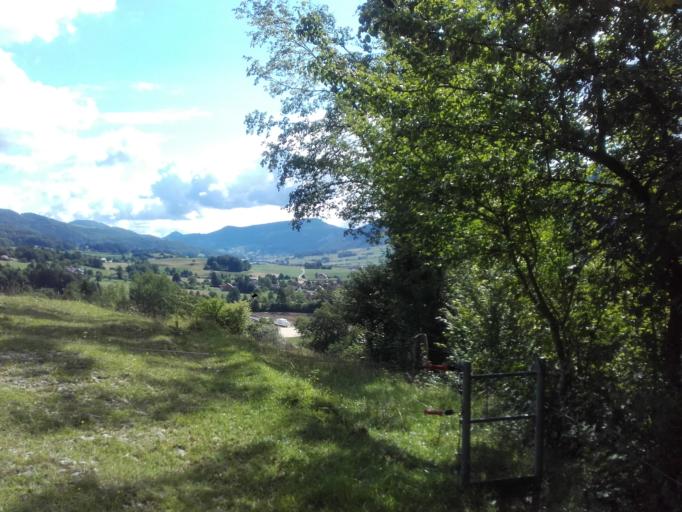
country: CH
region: Solothurn
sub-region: Bezirk Thal
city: Matzendorf
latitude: 47.3059
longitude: 7.5948
